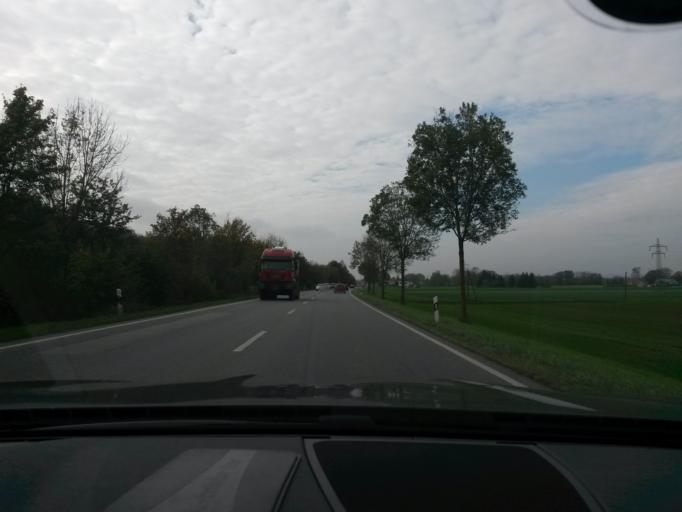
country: DE
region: Bavaria
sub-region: Lower Bavaria
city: Eching
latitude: 48.4982
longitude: 12.0552
